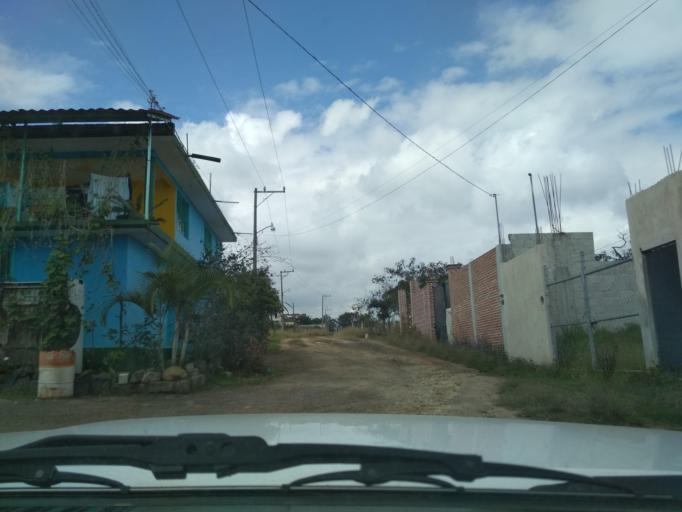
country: MX
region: Veracruz
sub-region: Emiliano Zapata
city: Jacarandas
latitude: 19.4962
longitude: -96.8393
